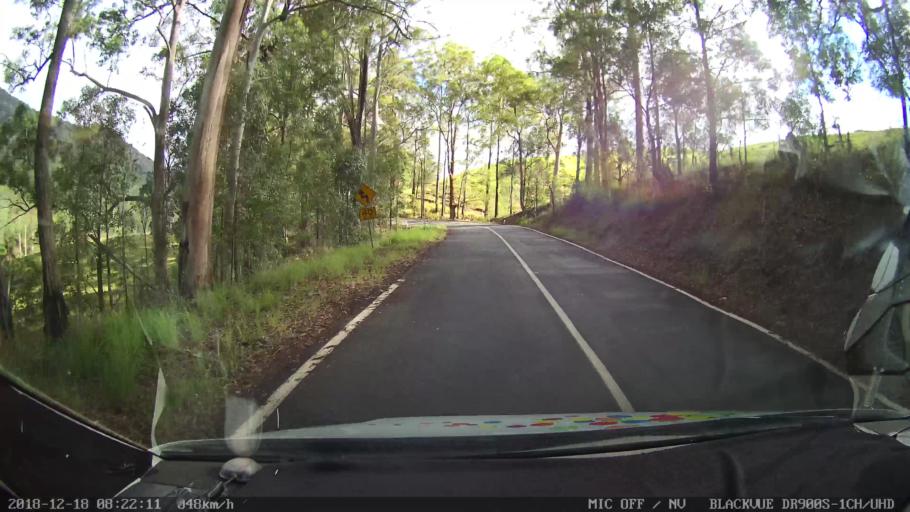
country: AU
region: New South Wales
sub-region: Kyogle
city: Kyogle
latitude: -28.3267
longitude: 152.7248
